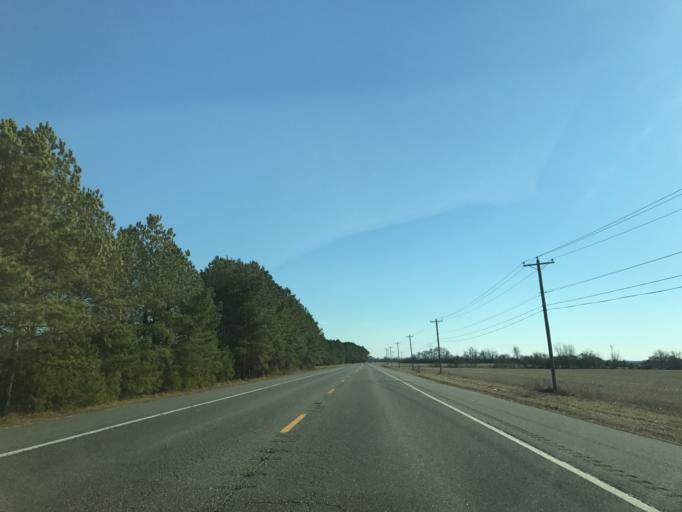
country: US
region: Maryland
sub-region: Queen Anne's County
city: Centreville
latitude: 38.9824
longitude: -76.0711
